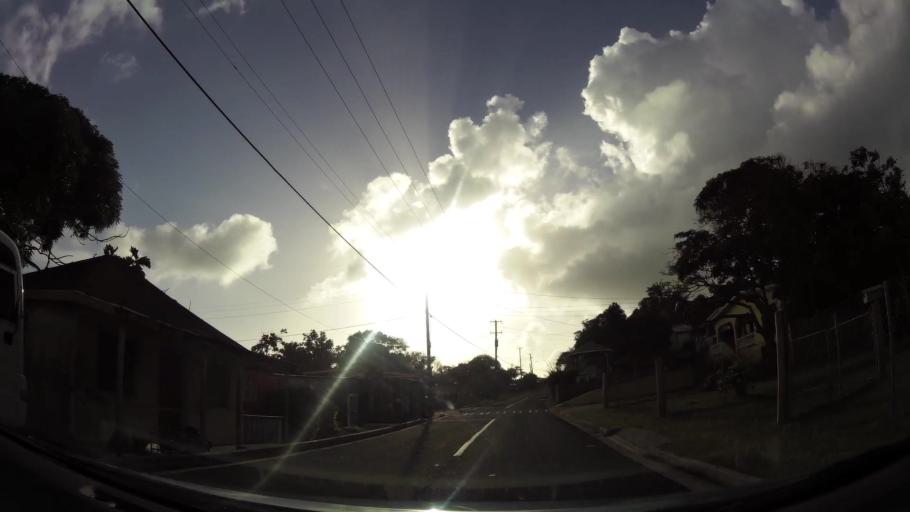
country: KN
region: Saint George Gingerland
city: Market Shop
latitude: 17.1307
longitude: -62.5801
